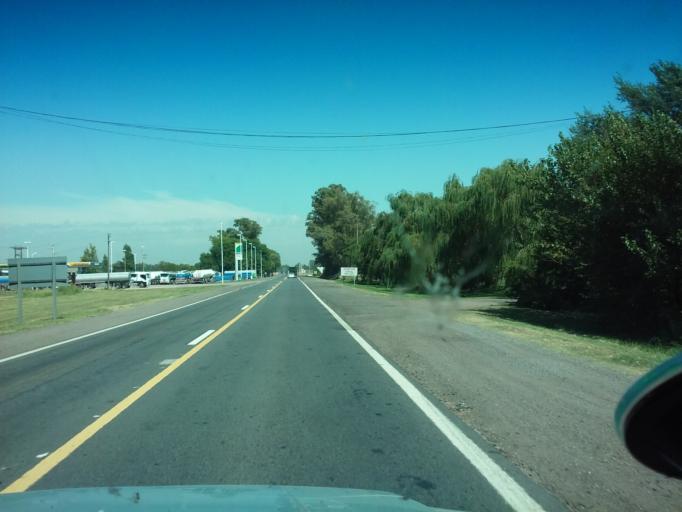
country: AR
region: Buenos Aires
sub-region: Partido de Nueve de Julio
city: Nueve de Julio
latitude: -35.4877
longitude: -60.8875
